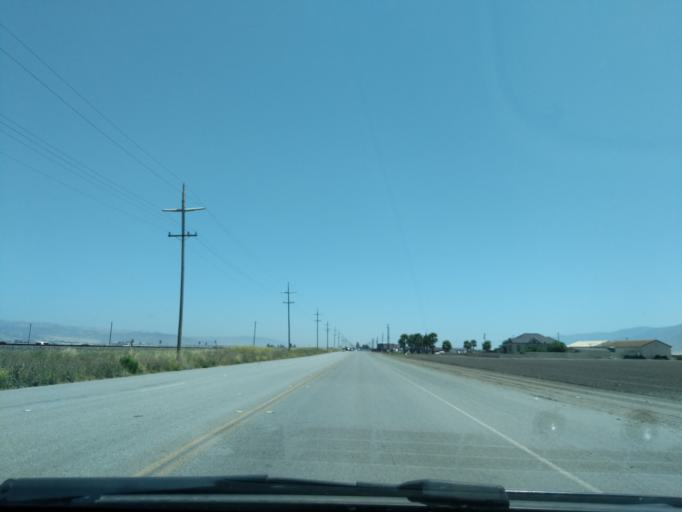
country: US
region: California
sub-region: Monterey County
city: Salinas
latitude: 36.6398
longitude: -121.6052
